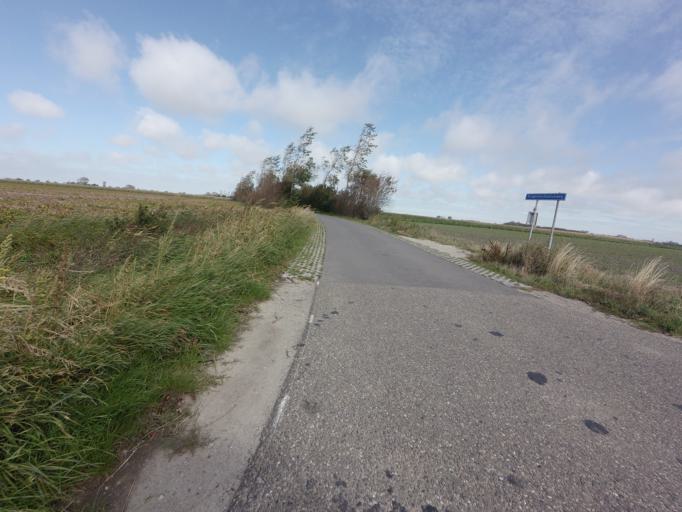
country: NL
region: Zeeland
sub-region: Gemeente Middelburg
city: Middelburg
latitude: 51.5134
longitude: 3.5373
